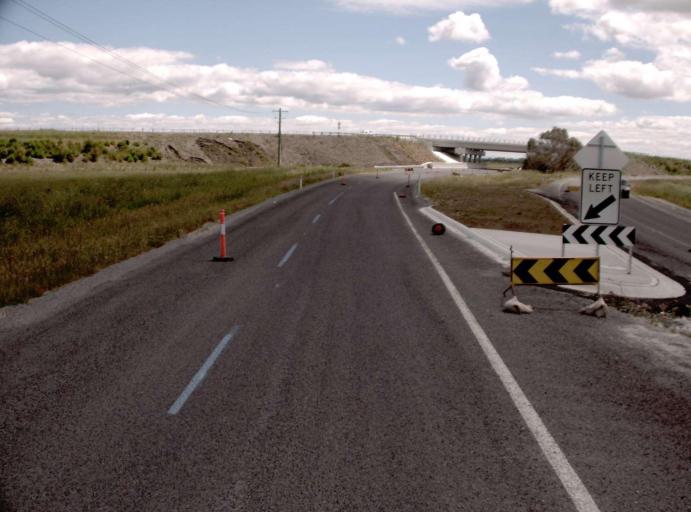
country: AU
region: Victoria
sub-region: Bass Coast
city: North Wonthaggi
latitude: -38.5098
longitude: 145.4500
